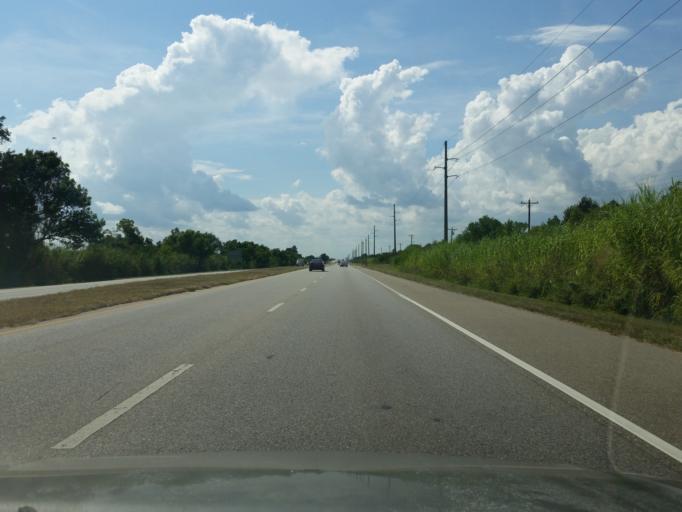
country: US
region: Alabama
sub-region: Baldwin County
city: Spanish Fort
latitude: 30.6700
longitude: -87.9367
